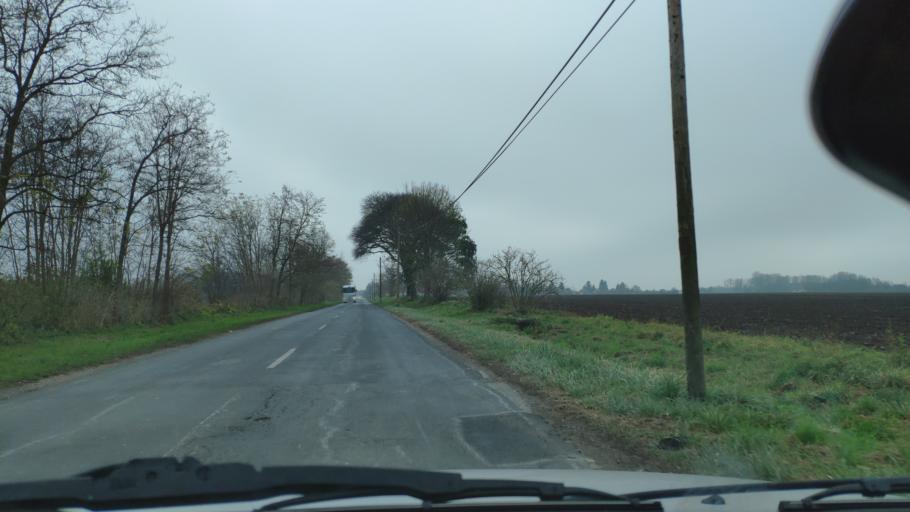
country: HU
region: Somogy
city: Balatonbereny
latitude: 46.6802
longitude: 17.2853
